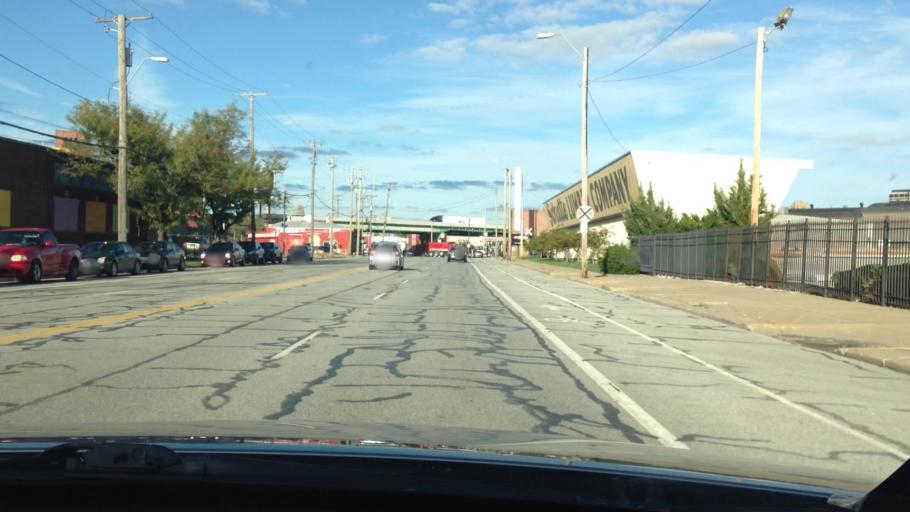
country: US
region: Kansas
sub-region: Johnson County
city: Westwood
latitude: 39.0743
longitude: -94.6047
